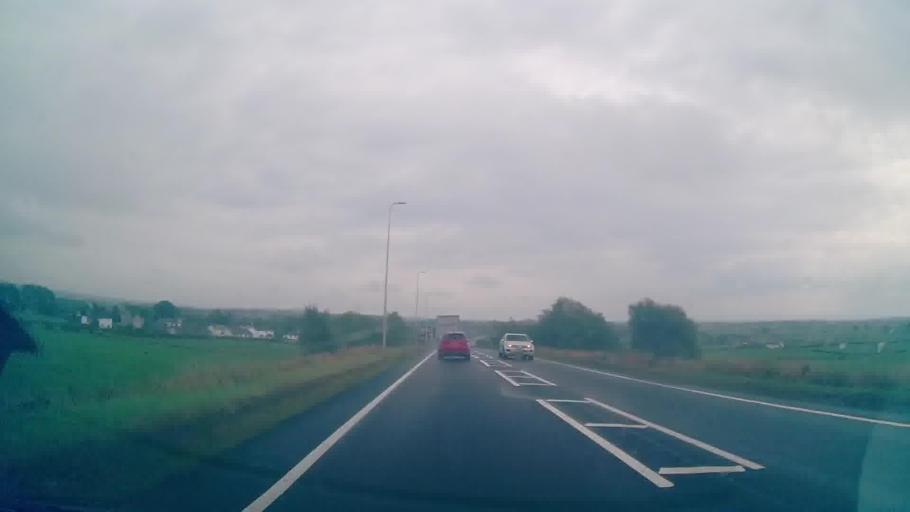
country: GB
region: Scotland
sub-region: Dumfries and Galloway
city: Lochmaben
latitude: 55.0335
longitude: -3.4109
